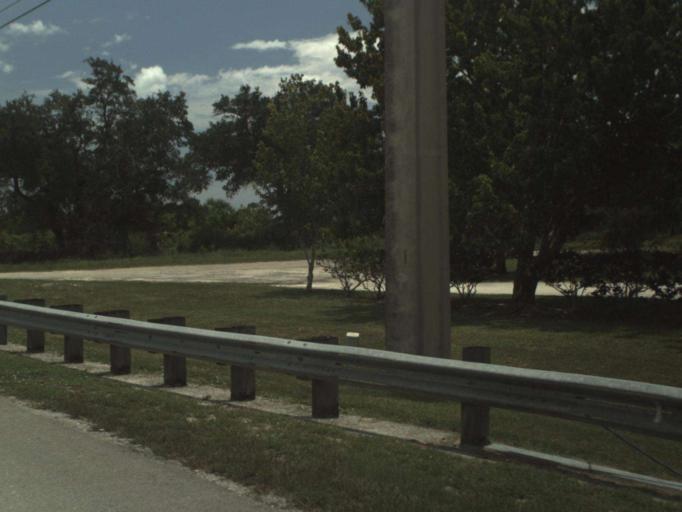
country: US
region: Florida
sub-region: Saint Lucie County
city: Lakewood Park
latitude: 27.5211
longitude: -80.4073
